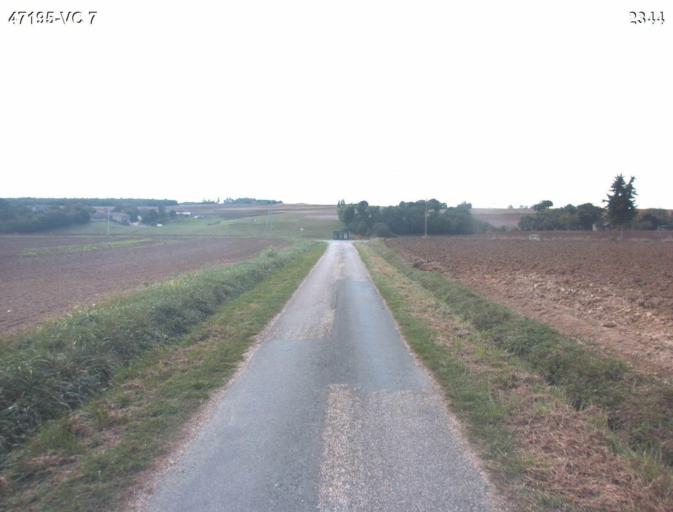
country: FR
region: Aquitaine
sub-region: Departement du Lot-et-Garonne
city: Nerac
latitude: 44.0976
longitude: 0.3368
